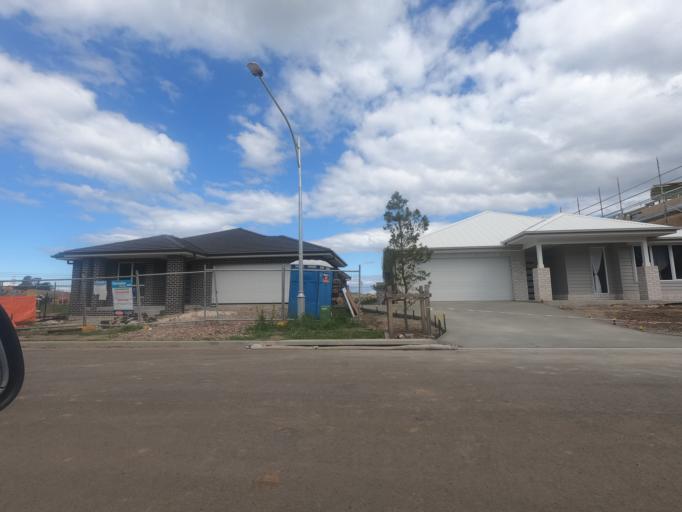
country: AU
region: New South Wales
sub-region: Wollongong
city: Dapto
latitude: -34.4803
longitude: 150.7675
